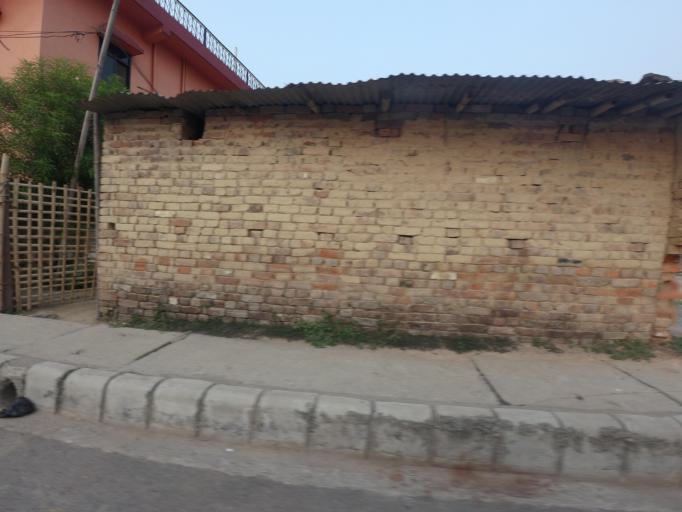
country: NP
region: Western Region
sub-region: Lumbini Zone
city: Bhairahawa
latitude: 27.5080
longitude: 83.4473
